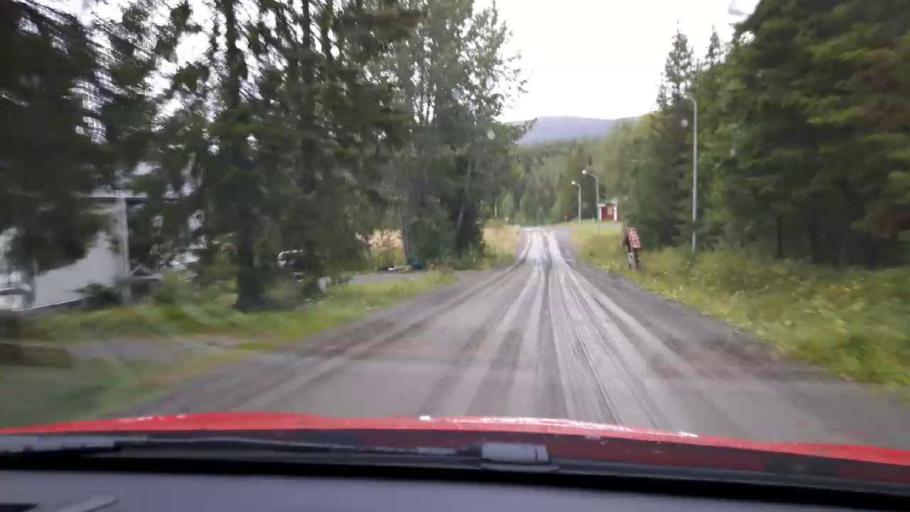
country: SE
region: Jaemtland
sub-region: Are Kommun
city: Are
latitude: 63.4743
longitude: 12.8082
